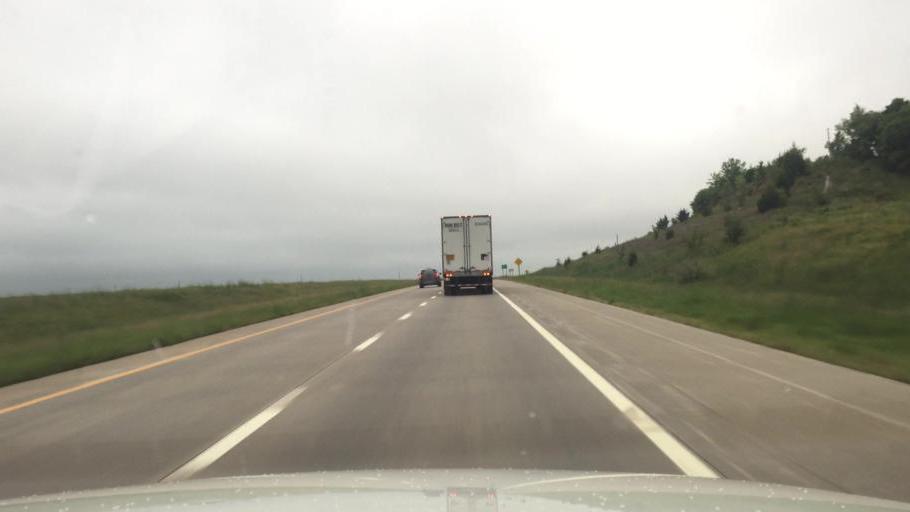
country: US
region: Kansas
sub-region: Montgomery County
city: Cherryvale
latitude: 37.2145
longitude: -95.5853
